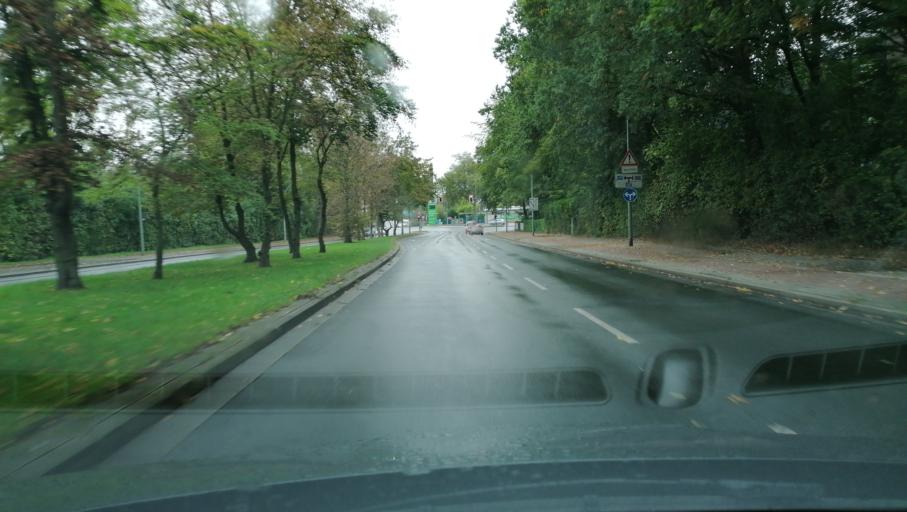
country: DE
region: North Rhine-Westphalia
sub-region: Regierungsbezirk Munster
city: Gelsenkirchen
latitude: 51.5229
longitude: 7.0641
